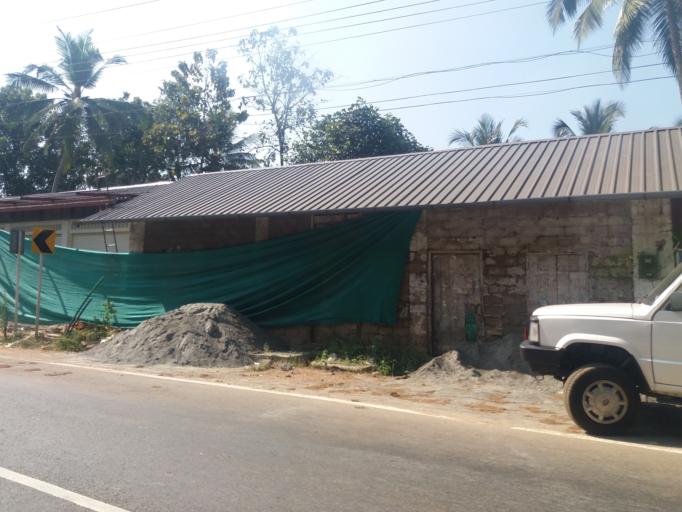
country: IN
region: Kerala
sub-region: Ernakulam
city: Muvattupuzha
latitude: 9.8872
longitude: 76.6977
